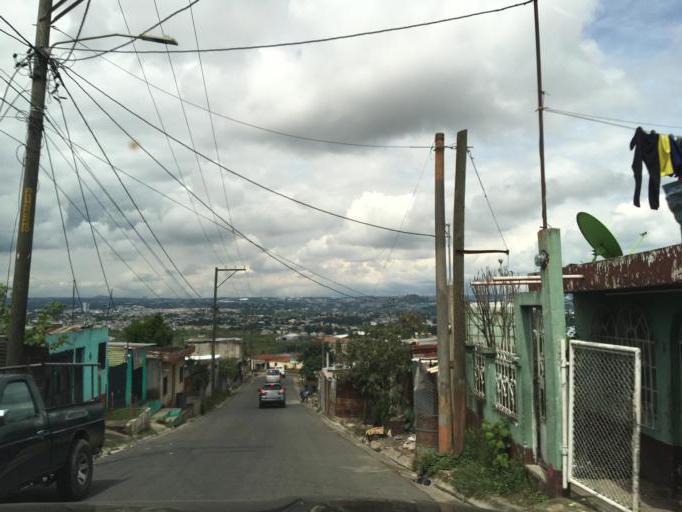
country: GT
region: Guatemala
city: Villa Nueva
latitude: 14.5032
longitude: -90.5899
